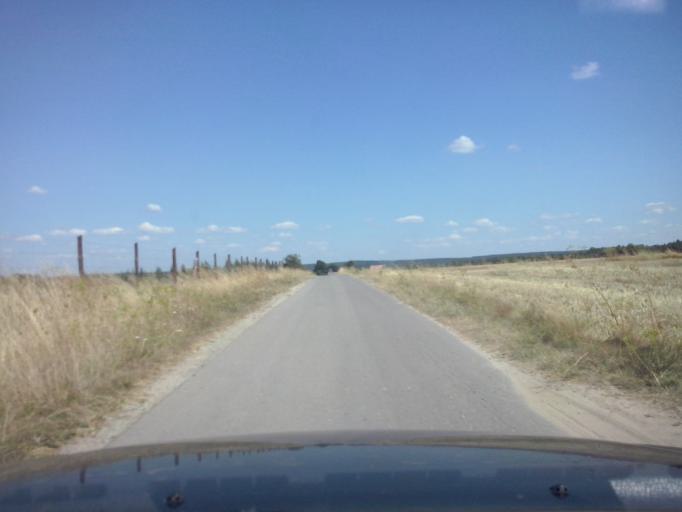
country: PL
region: Swietokrzyskie
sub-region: Powiat buski
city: Gnojno
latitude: 50.5935
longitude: 20.8951
